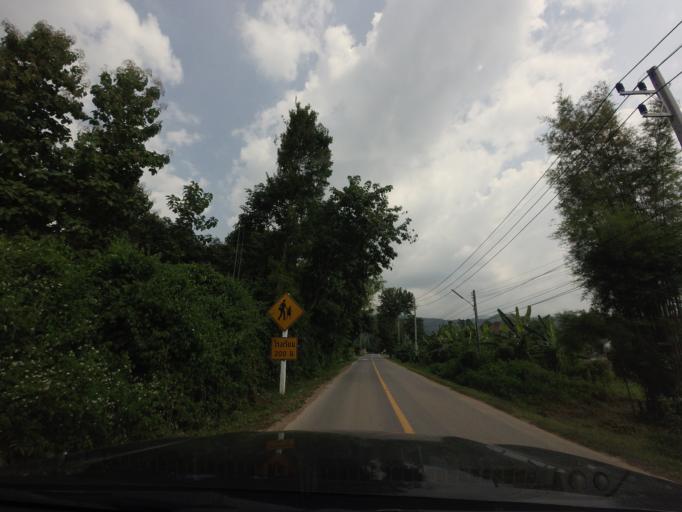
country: TH
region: Nan
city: Pua
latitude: 19.1769
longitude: 100.9498
